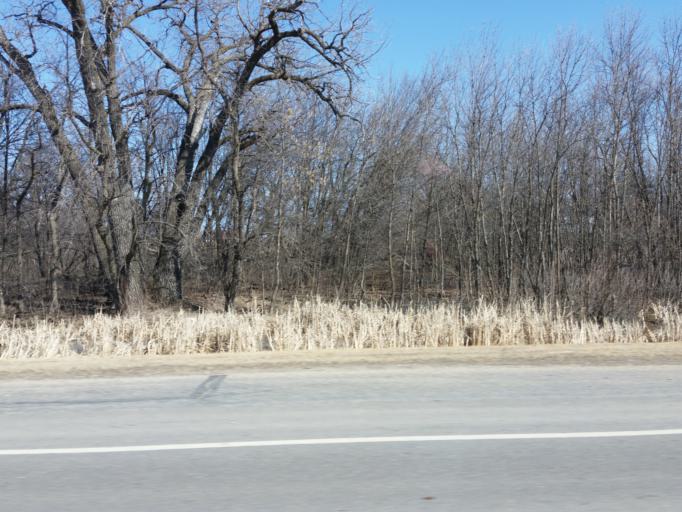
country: US
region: North Dakota
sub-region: Walsh County
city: Grafton
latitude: 48.2834
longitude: -97.3698
